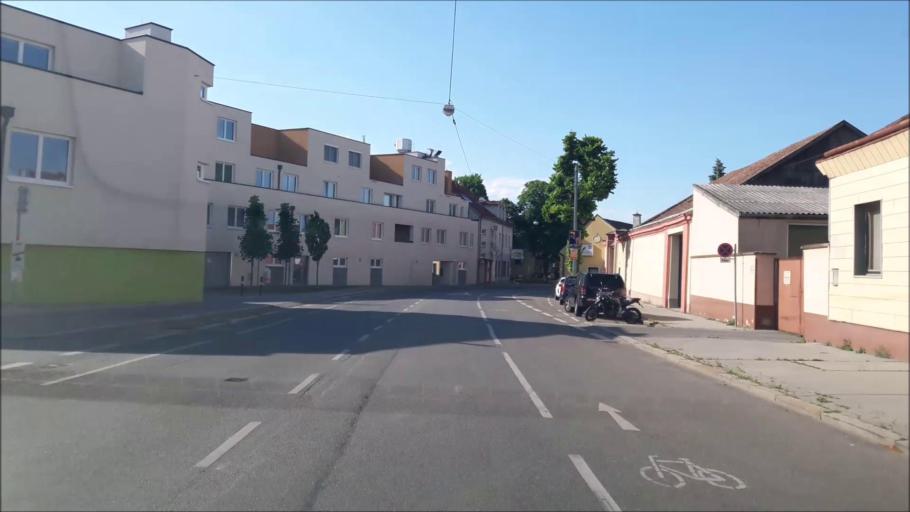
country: AT
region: Lower Austria
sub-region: Politischer Bezirk Wien-Umgebung
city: Leopoldsdorf
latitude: 48.1376
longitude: 16.3831
